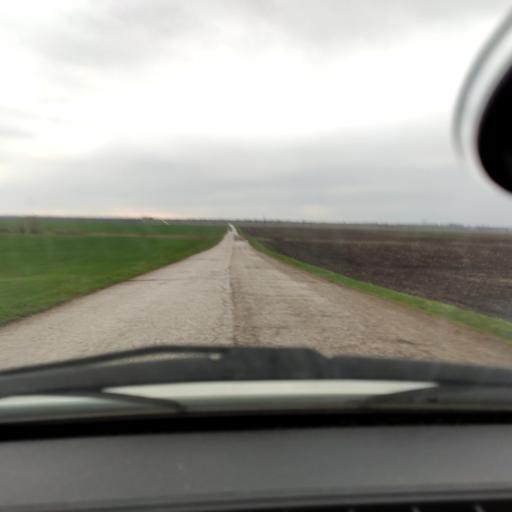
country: RU
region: Bashkortostan
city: Tolbazy
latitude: 54.1693
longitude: 55.9414
